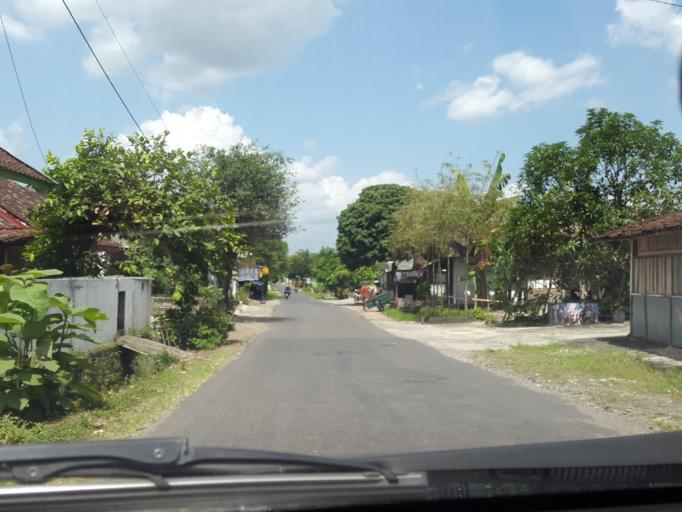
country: ID
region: Central Java
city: Selogiri
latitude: -7.8664
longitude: 110.7410
